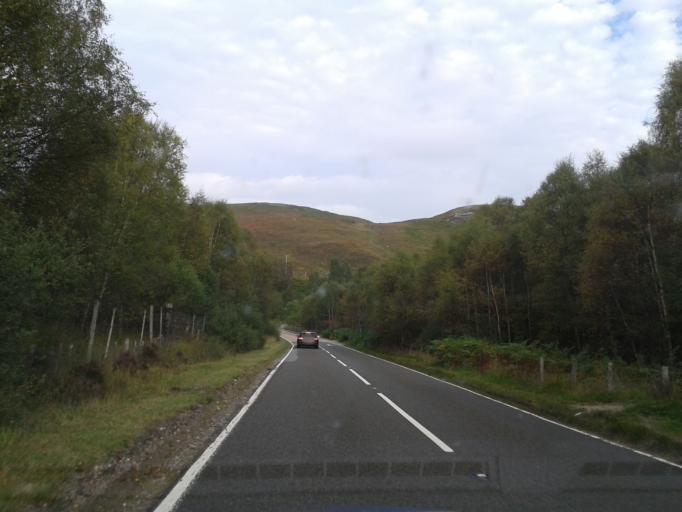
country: GB
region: Scotland
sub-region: Highland
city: Spean Bridge
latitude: 57.1446
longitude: -4.9583
